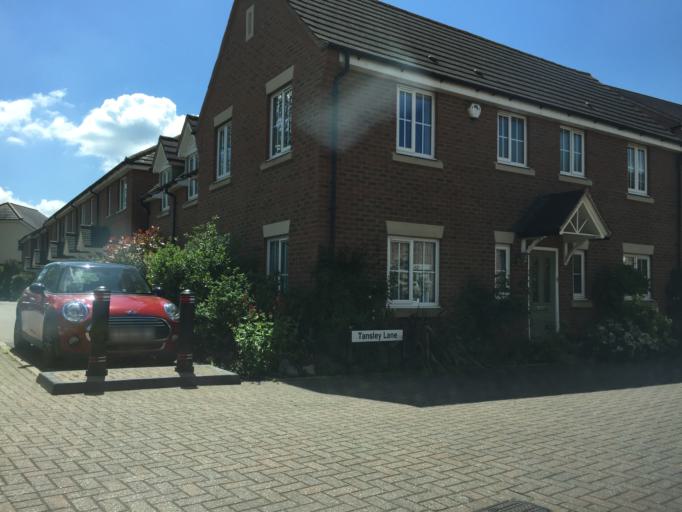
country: GB
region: England
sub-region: Milton Keynes
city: Woburn Sands
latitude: 52.0160
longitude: -0.6519
